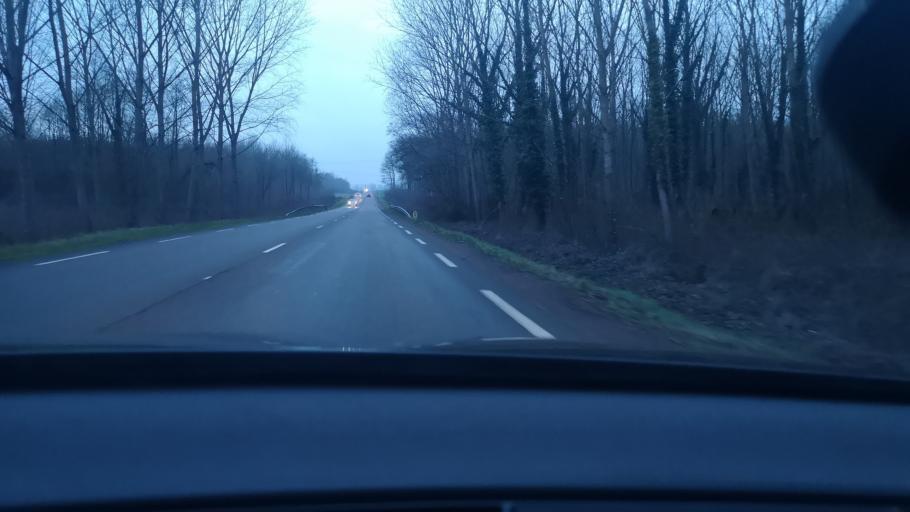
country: FR
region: Bourgogne
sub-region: Departement de Saone-et-Loire
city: Verdun-sur-le-Doubs
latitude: 47.0052
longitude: 5.0174
